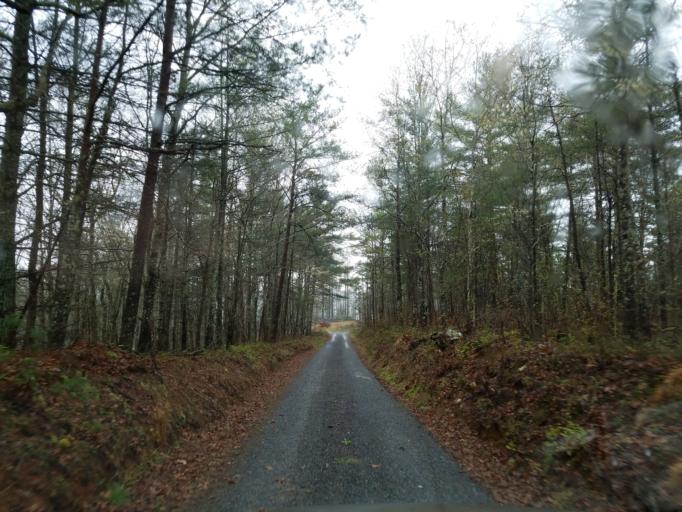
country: US
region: Georgia
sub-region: Fannin County
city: Blue Ridge
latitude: 34.8392
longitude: -84.2347
